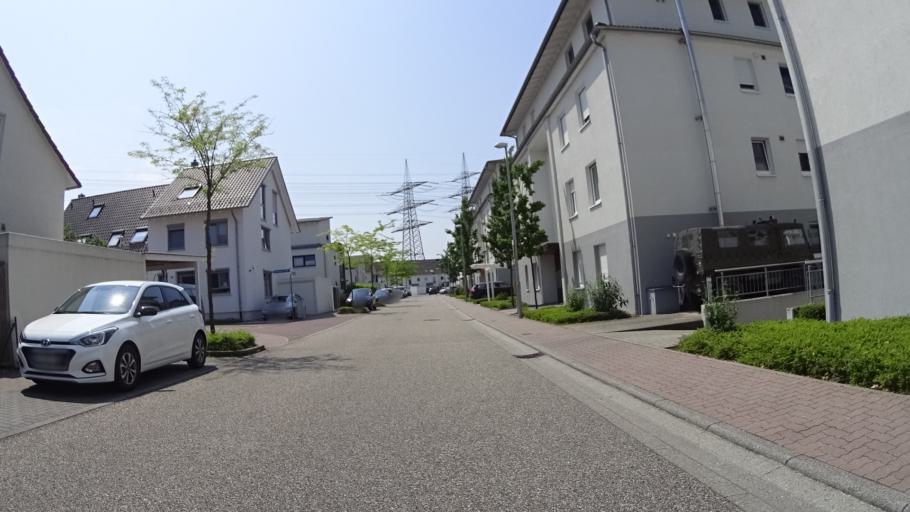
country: DE
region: Baden-Wuerttemberg
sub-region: Karlsruhe Region
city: Eggenstein-Leopoldshafen
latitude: 49.0913
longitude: 8.4051
